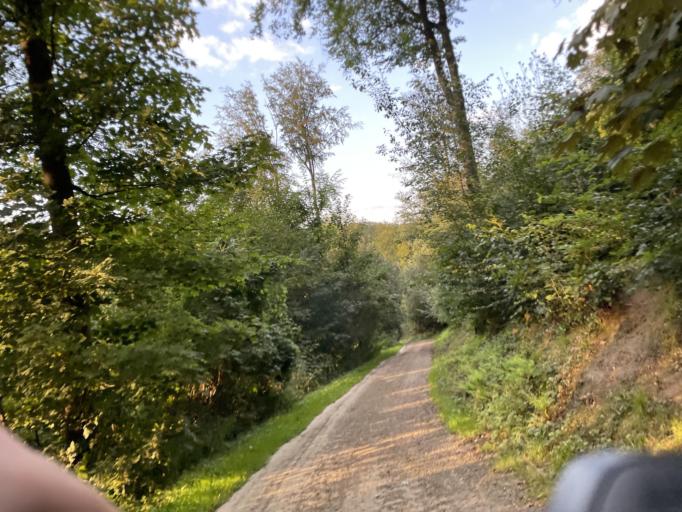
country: DE
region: North Rhine-Westphalia
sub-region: Regierungsbezirk Dusseldorf
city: Essen
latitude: 51.4147
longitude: 7.0489
